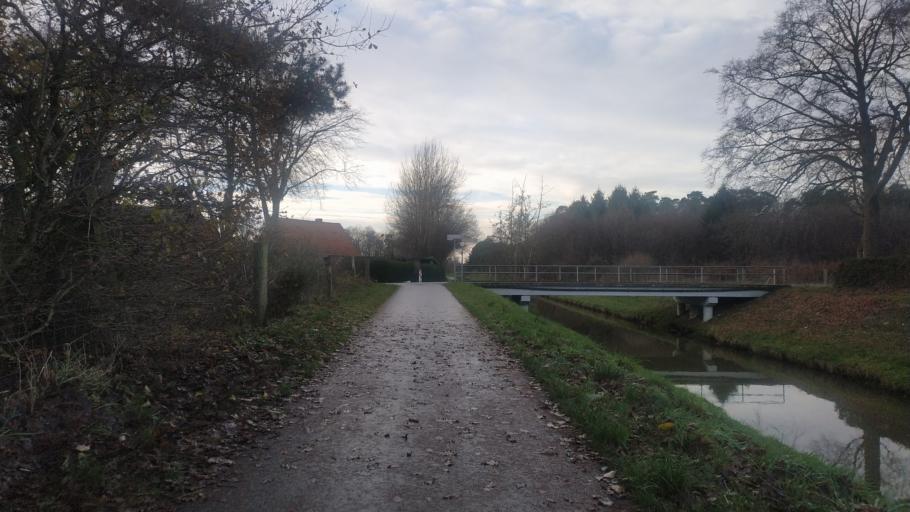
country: DE
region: North Rhine-Westphalia
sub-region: Regierungsbezirk Munster
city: Horstel
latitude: 52.2914
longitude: 7.6270
